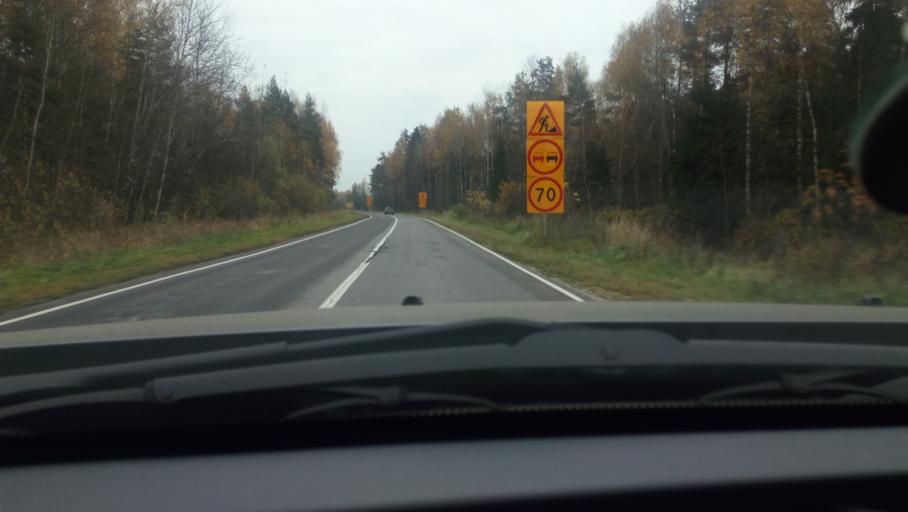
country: RU
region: Moskovskaya
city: Drezna
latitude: 55.7020
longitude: 38.8763
